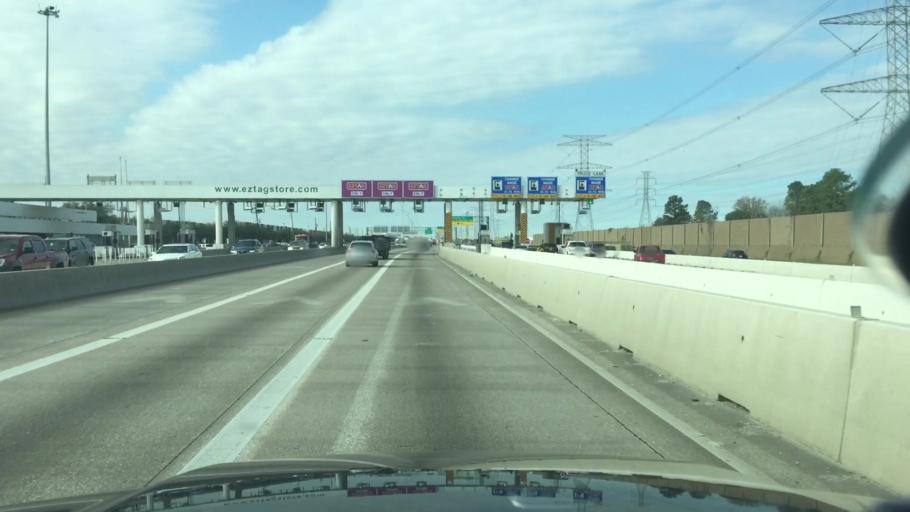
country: US
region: Texas
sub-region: Harris County
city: Hudson
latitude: 29.9377
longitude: -95.4706
